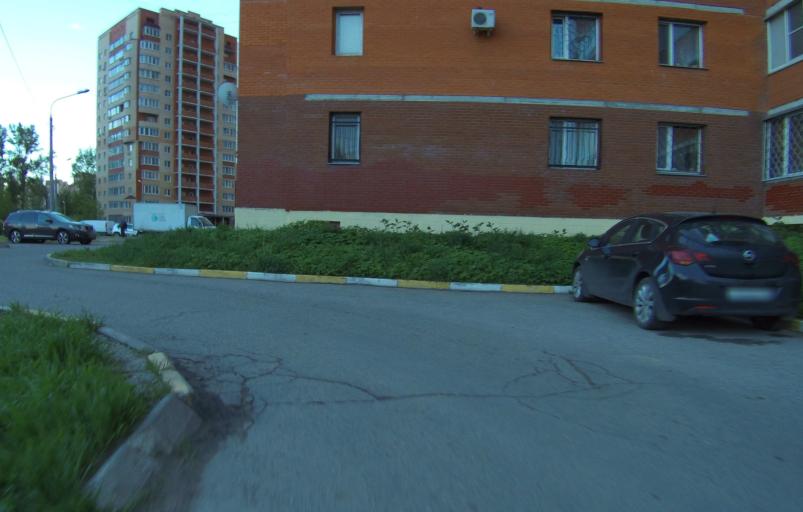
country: RU
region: Moskovskaya
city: Ramenskoye
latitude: 55.5800
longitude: 38.2489
